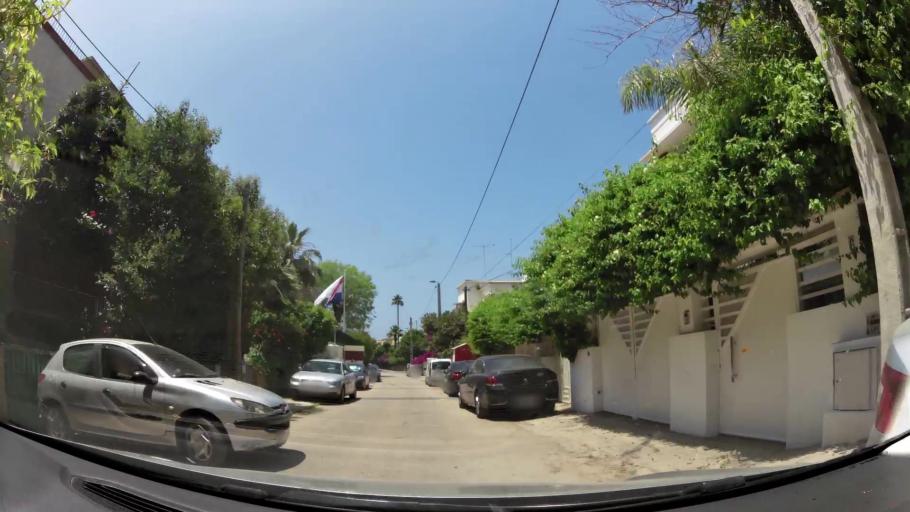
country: MA
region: Rabat-Sale-Zemmour-Zaer
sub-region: Rabat
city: Rabat
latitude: 34.0161
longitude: -6.8231
